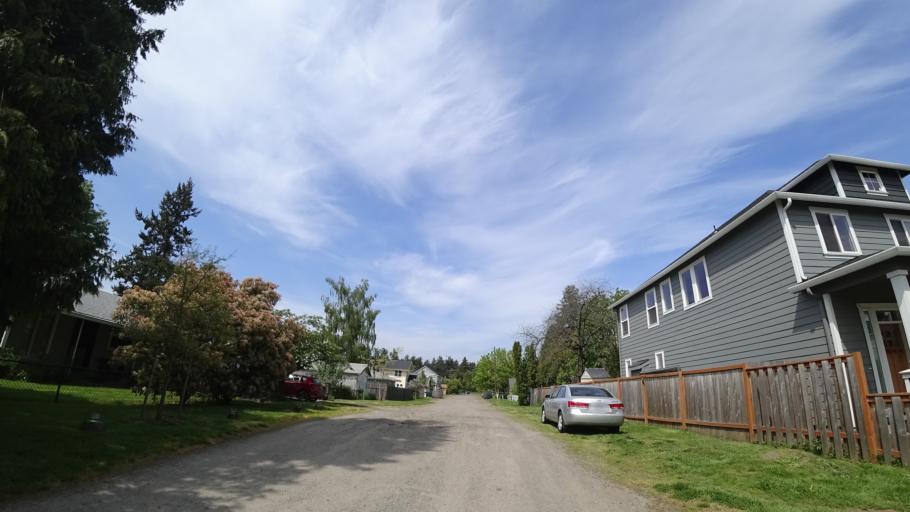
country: US
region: Oregon
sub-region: Clackamas County
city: Milwaukie
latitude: 45.4701
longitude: -122.6073
